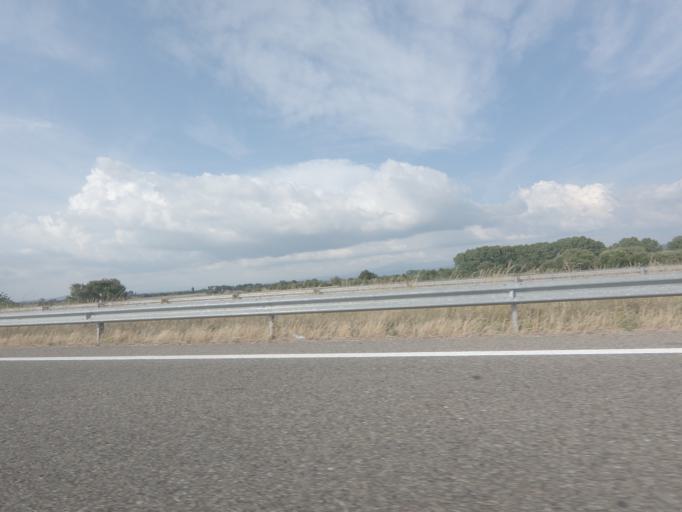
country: ES
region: Galicia
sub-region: Provincia de Ourense
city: Xinzo de Limia
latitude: 42.0866
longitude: -7.7195
